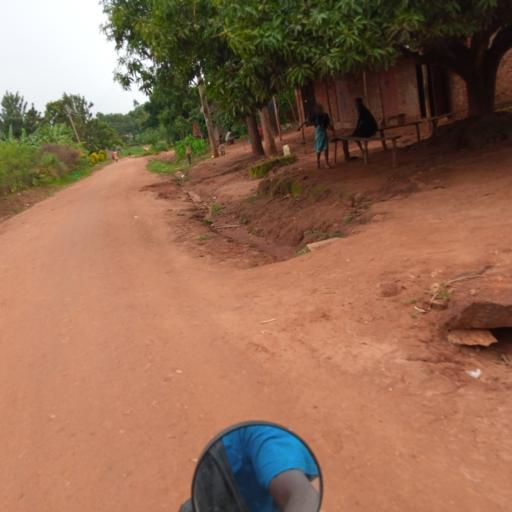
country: UG
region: Eastern Region
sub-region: Mbale District
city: Mbale
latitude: 1.1252
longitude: 34.1766
